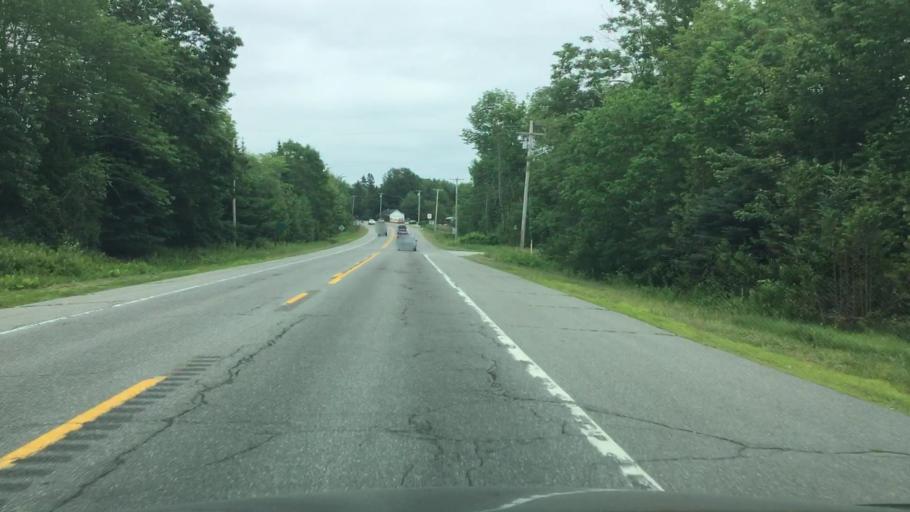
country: US
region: Maine
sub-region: Waldo County
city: Stockton Springs
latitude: 44.4932
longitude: -68.8503
